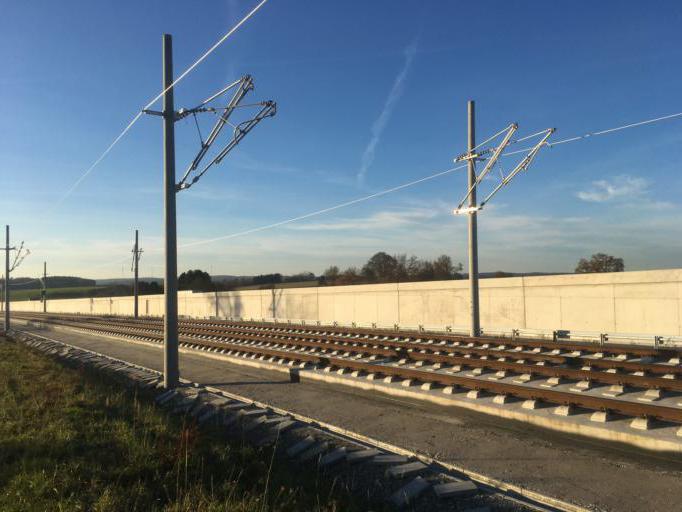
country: DE
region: Baden-Wuerttemberg
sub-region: Tuebingen Region
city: Nellingen
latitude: 48.5199
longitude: 9.8027
